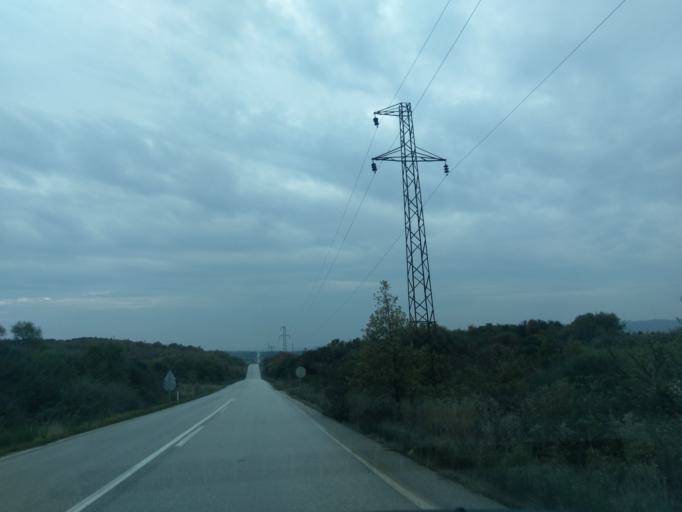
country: TR
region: Istanbul
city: Canta
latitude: 41.1582
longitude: 28.1068
